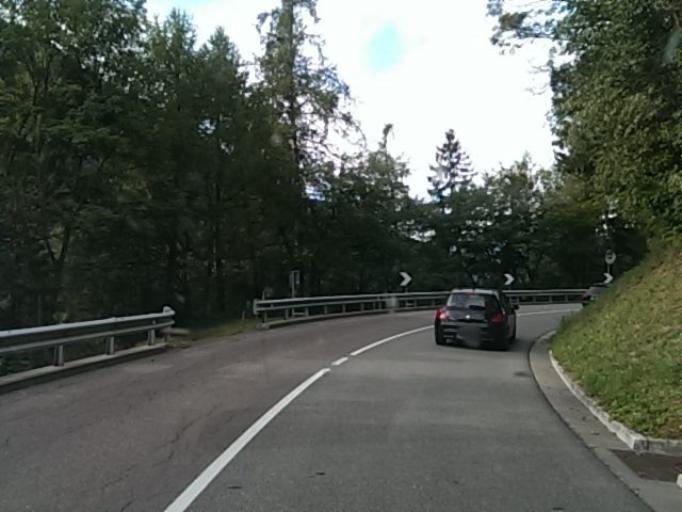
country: IT
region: Trentino-Alto Adige
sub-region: Bolzano
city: San Pancrazio
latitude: 46.6073
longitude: 11.1125
